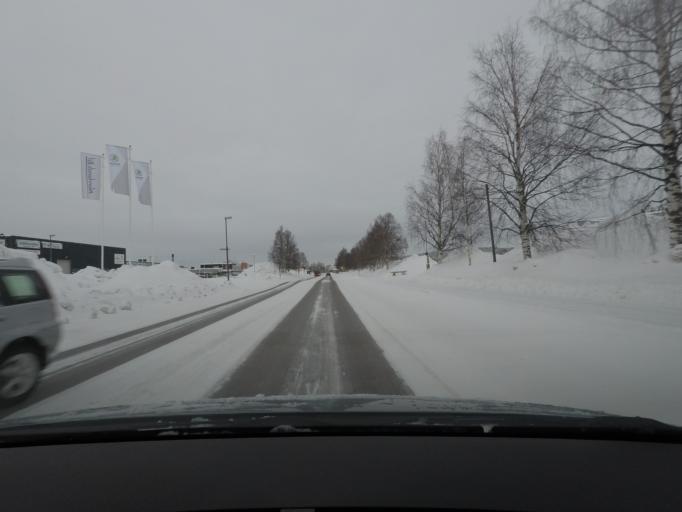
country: SE
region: Norrbotten
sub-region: Lulea Kommun
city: Lulea
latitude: 65.5965
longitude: 22.1465
